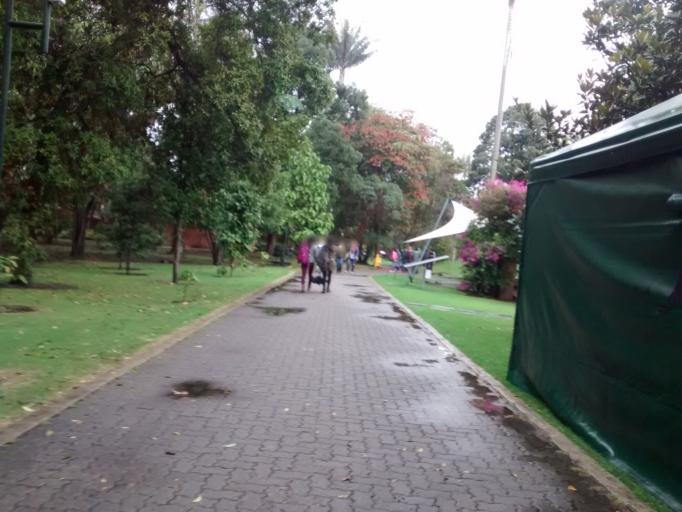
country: CO
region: Bogota D.C.
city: Bogota
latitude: 4.6689
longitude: -74.0993
